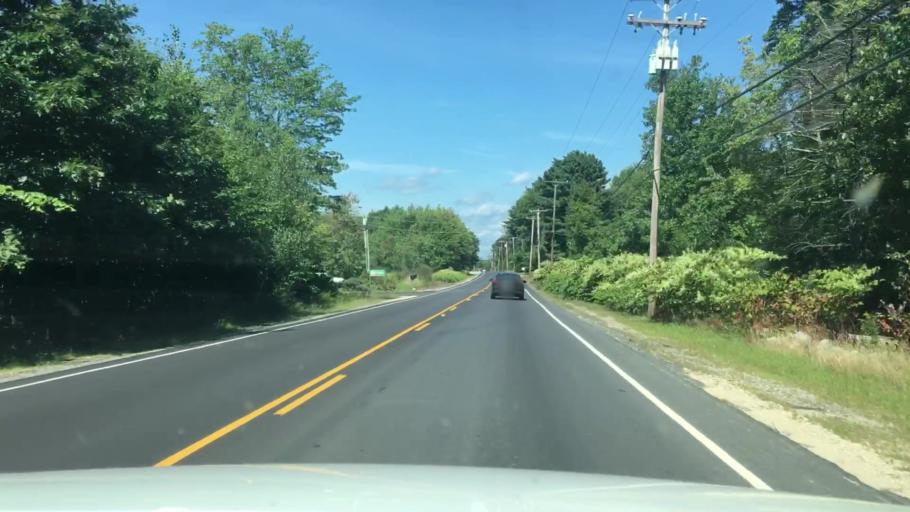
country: US
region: Maine
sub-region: Cumberland County
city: Cumberland Center
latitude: 43.8419
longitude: -70.3218
